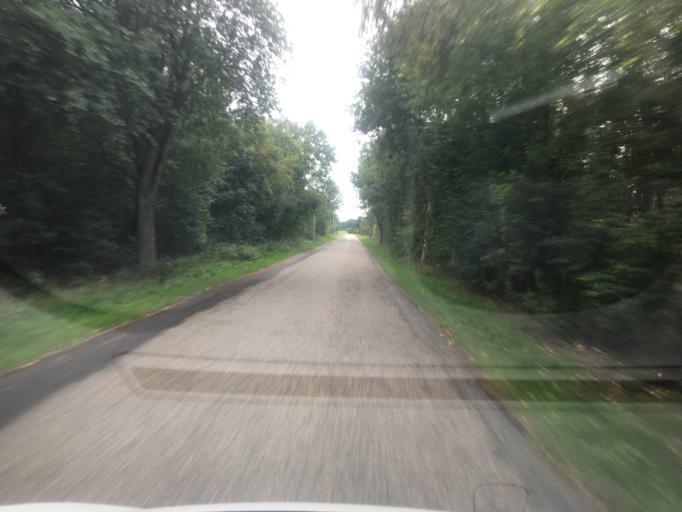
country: DK
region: South Denmark
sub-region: Tonder Kommune
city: Tonder
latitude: 54.9554
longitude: 8.9109
